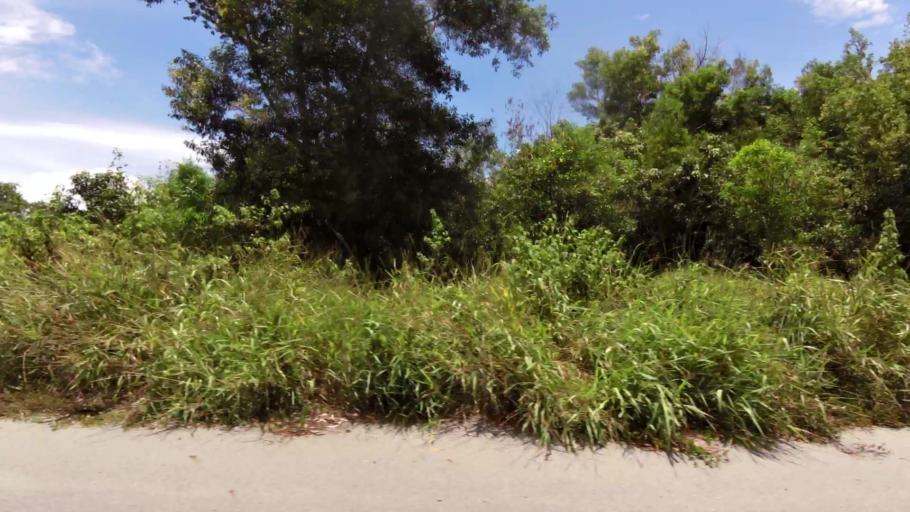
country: BN
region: Brunei and Muara
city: Bandar Seri Begawan
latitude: 4.9426
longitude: 114.8873
